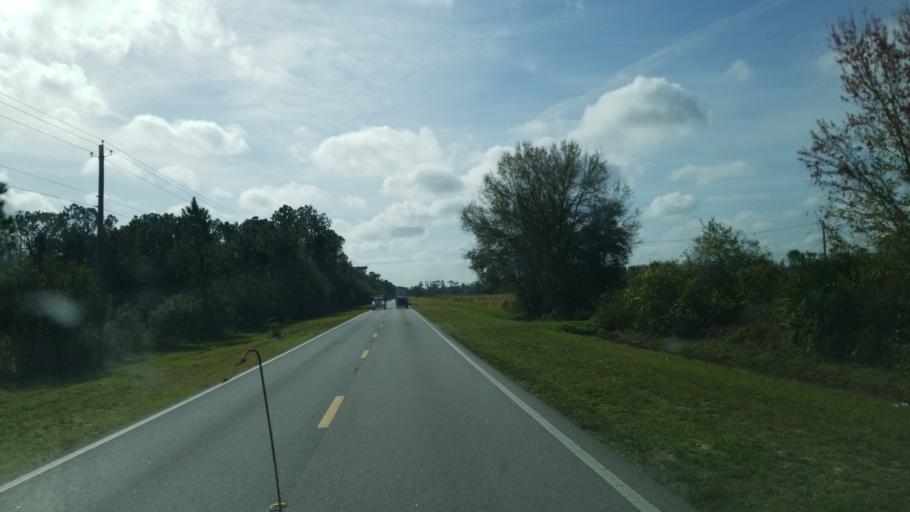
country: US
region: Florida
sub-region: Polk County
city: Polk City
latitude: 28.2454
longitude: -81.7595
